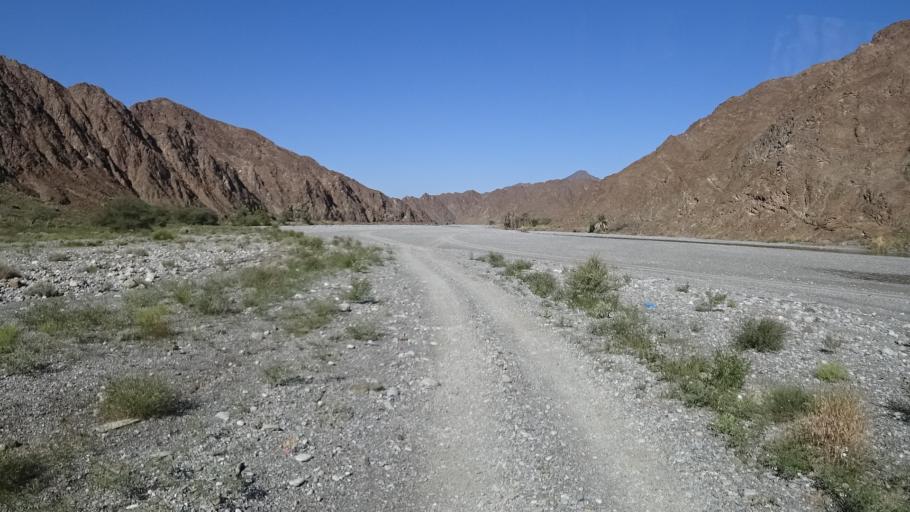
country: OM
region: Al Batinah
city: Bayt al `Awabi
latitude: 23.4037
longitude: 57.6659
